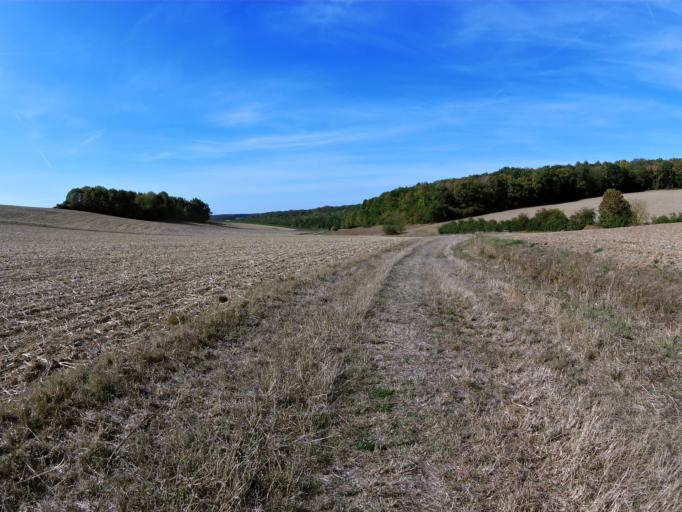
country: DE
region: Bavaria
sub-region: Regierungsbezirk Unterfranken
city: Eisingen
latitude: 49.7642
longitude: 9.8324
